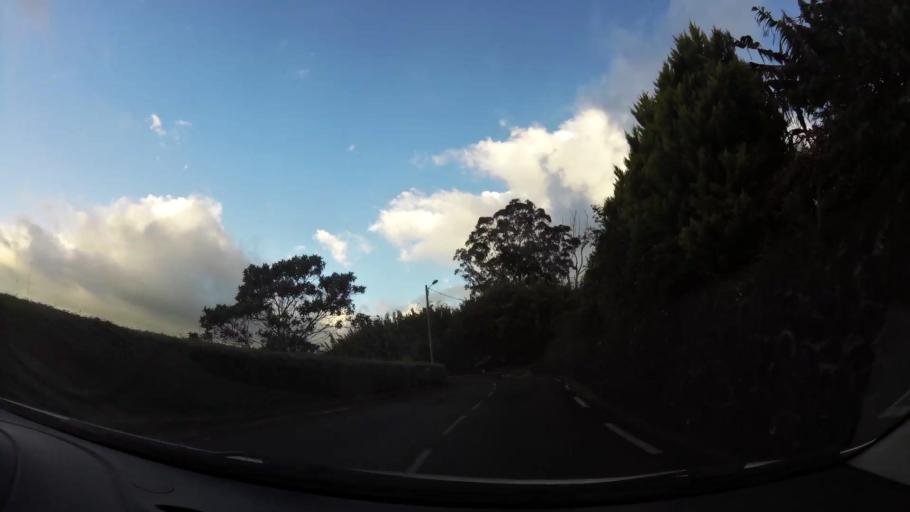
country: RE
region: Reunion
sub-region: Reunion
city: Saint-Denis
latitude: -20.9189
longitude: 55.4384
